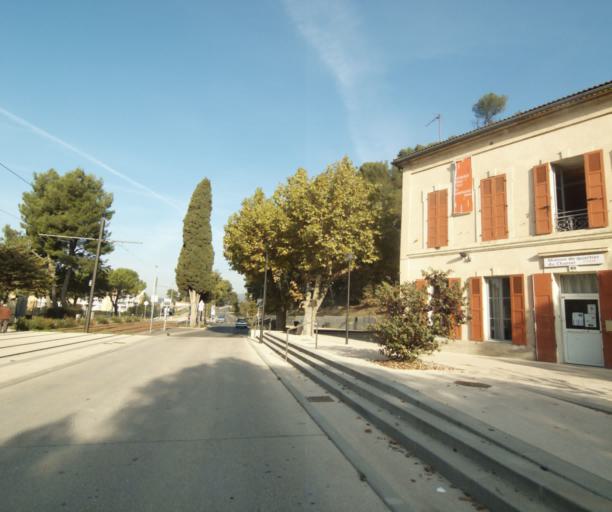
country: FR
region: Provence-Alpes-Cote d'Azur
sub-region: Departement des Bouches-du-Rhone
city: Aubagne
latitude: 43.2810
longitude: 5.5509
